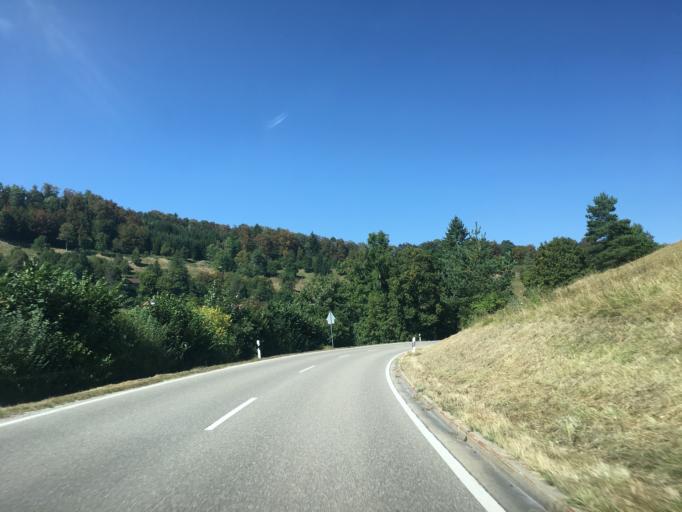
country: DE
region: Baden-Wuerttemberg
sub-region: Tuebingen Region
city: Hayingen
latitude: 48.3289
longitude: 9.4992
